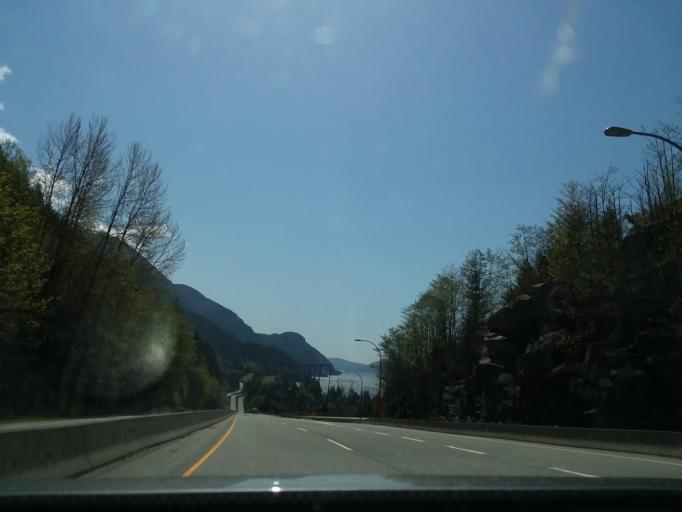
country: CA
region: British Columbia
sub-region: Greater Vancouver Regional District
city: Lions Bay
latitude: 49.5938
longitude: -123.2177
